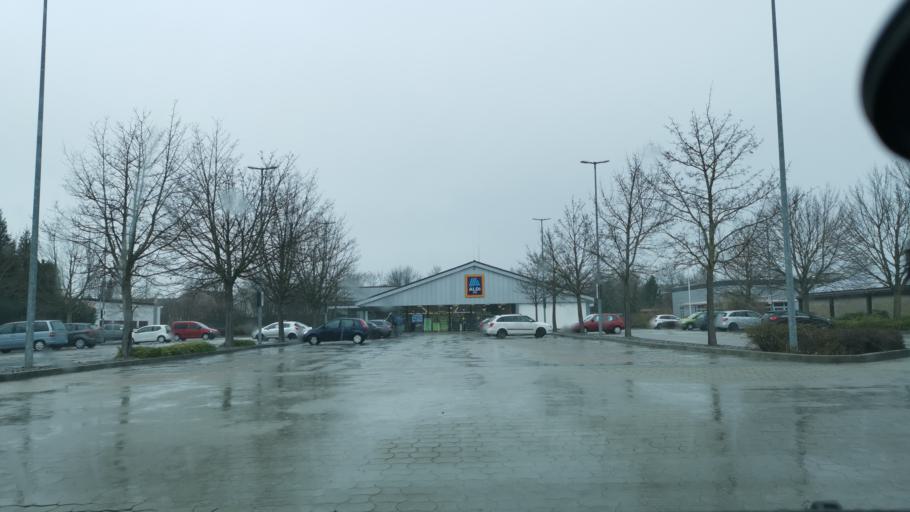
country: DE
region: Baden-Wuerttemberg
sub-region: Regierungsbezirk Stuttgart
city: Markgroningen
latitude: 48.9003
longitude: 9.0944
